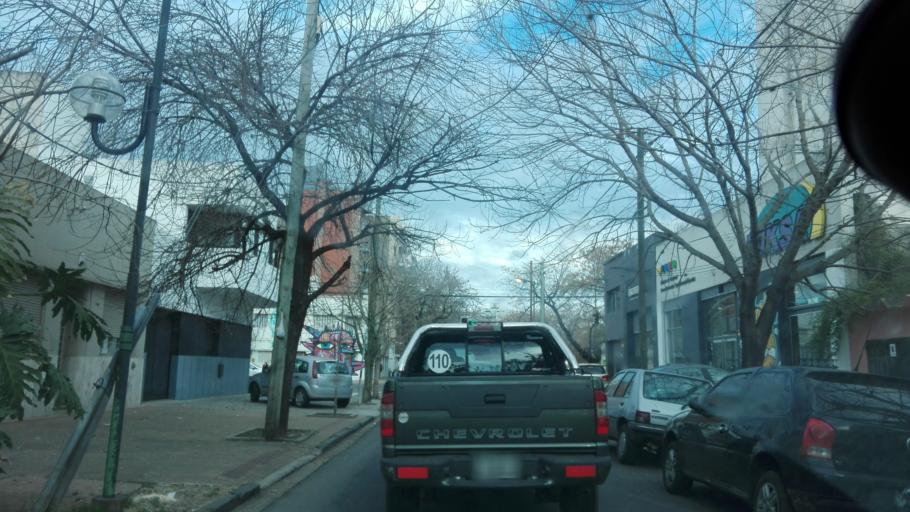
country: AR
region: Buenos Aires
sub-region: Partido de La Plata
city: La Plata
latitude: -34.9116
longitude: -57.9645
